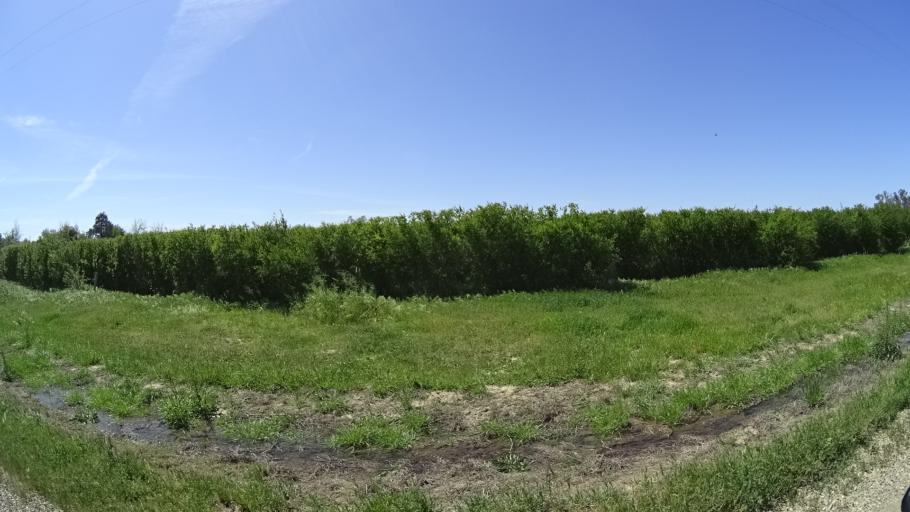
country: US
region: California
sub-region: Glenn County
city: Hamilton City
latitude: 39.7299
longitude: -122.0892
